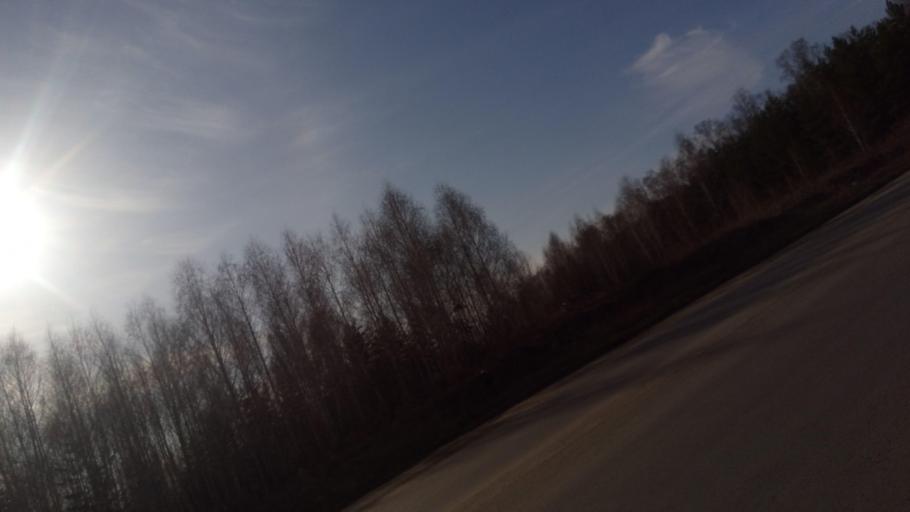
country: RU
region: Chelyabinsk
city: Sargazy
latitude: 55.1187
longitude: 61.2530
